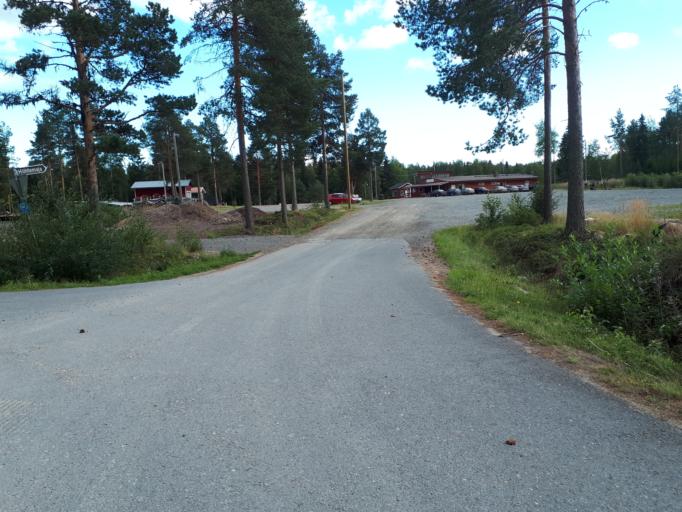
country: FI
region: Northern Ostrobothnia
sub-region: Oulunkaari
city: Ii
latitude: 65.3320
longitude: 25.3897
